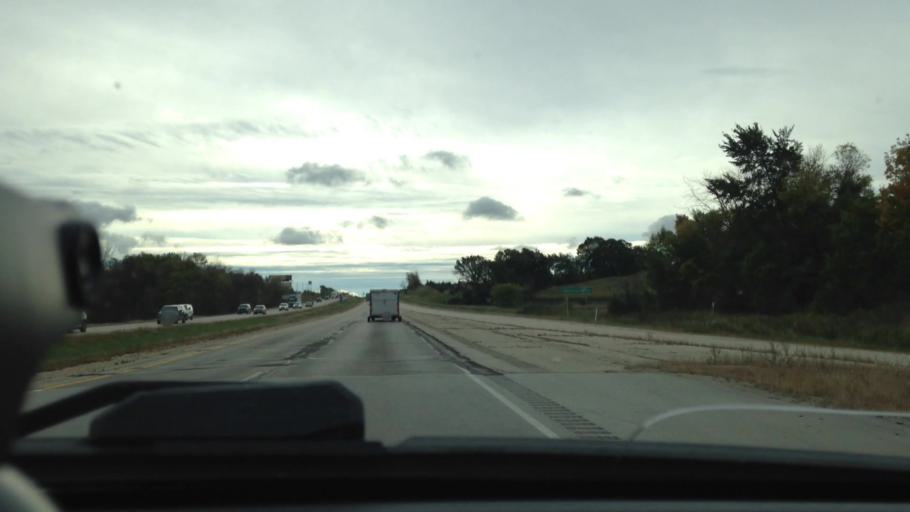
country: US
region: Wisconsin
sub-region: Dodge County
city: Theresa
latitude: 43.5348
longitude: -88.4007
